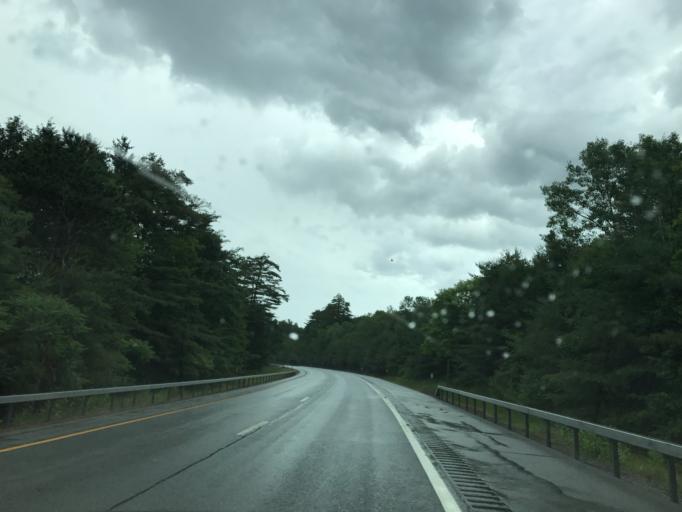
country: US
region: New York
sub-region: Warren County
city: Warrensburg
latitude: 43.5051
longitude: -73.7437
